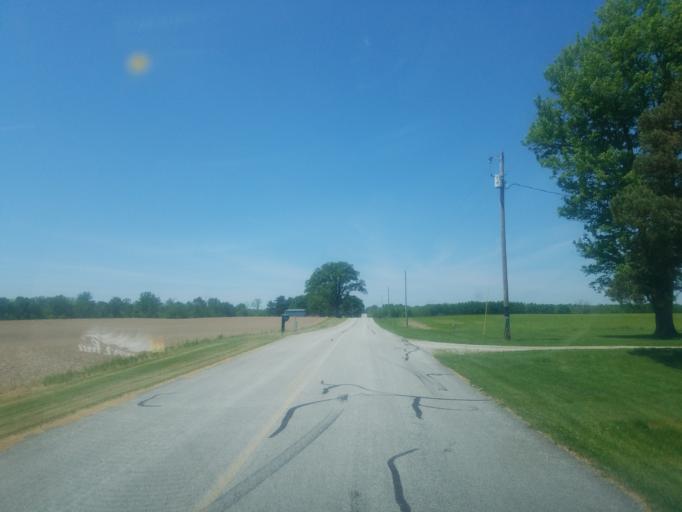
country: US
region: Ohio
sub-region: Huron County
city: New London
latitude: 41.1162
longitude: -82.4028
